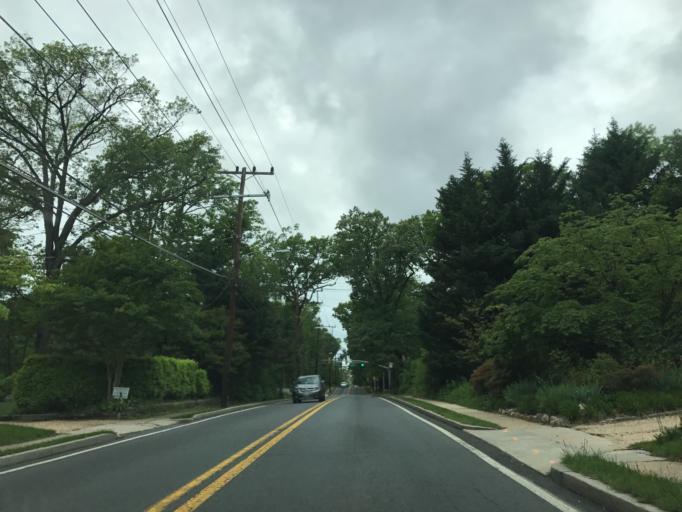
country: US
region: Maryland
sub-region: Montgomery County
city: Silver Spring
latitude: 38.9845
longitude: -77.0181
